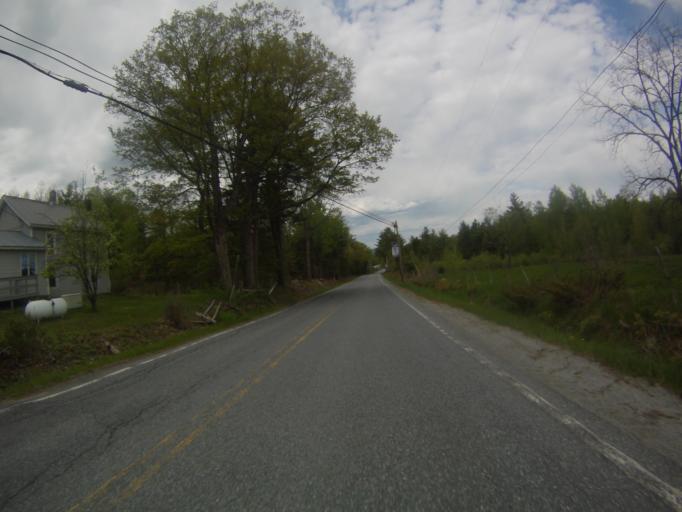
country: US
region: New York
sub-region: Essex County
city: Port Henry
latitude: 44.0090
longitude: -73.4997
